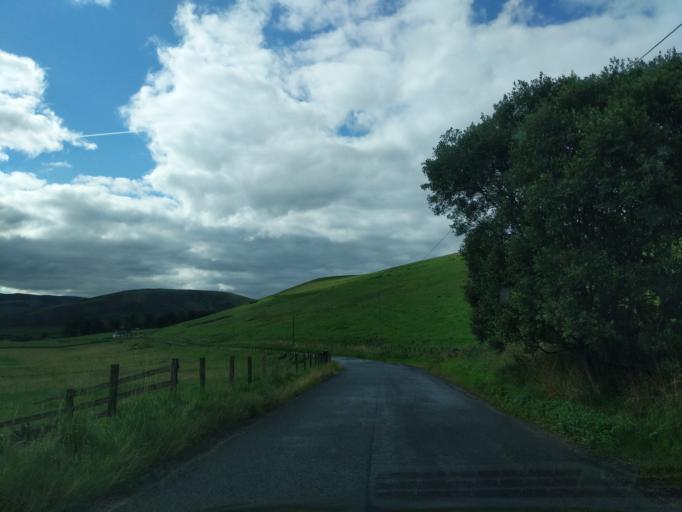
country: GB
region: Scotland
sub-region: The Scottish Borders
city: West Linton
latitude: 55.6848
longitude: -3.3342
